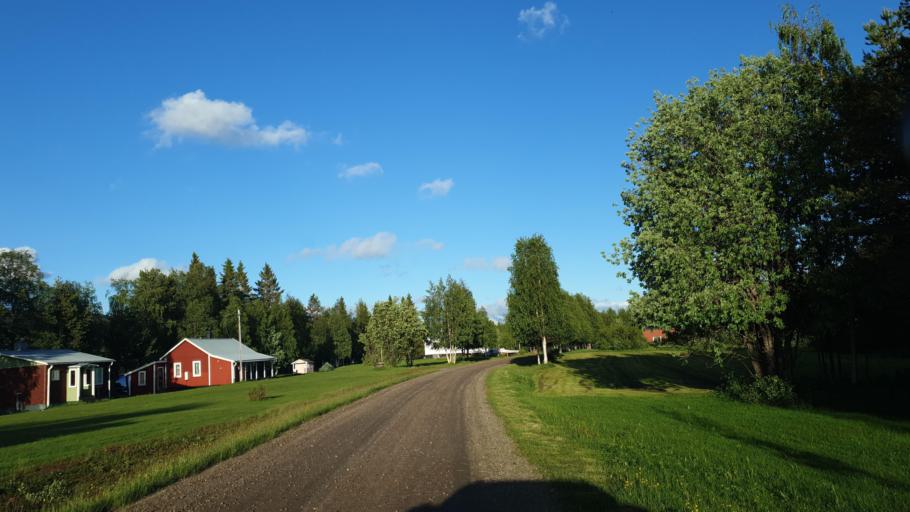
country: SE
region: Norrbotten
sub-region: Arvidsjaurs Kommun
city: Arvidsjaur
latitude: 65.7075
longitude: 18.7107
